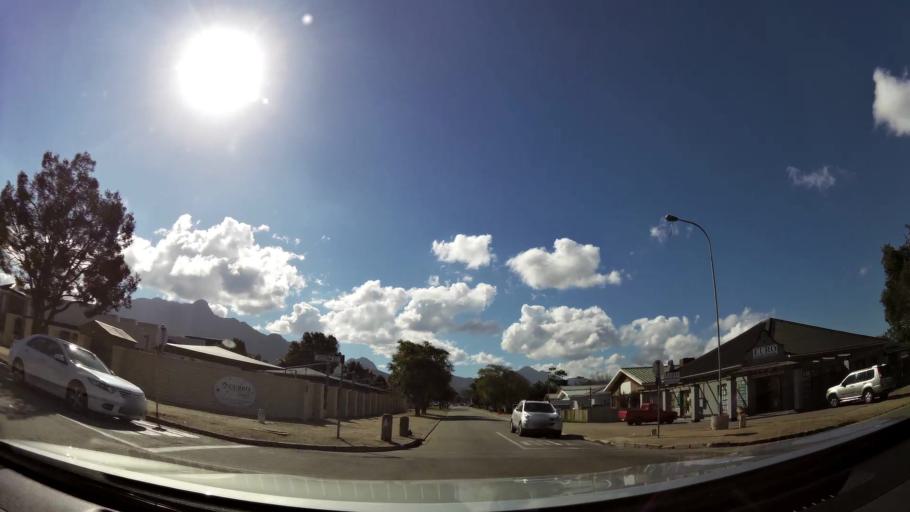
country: ZA
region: Western Cape
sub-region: Eden District Municipality
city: George
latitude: -33.9667
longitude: 22.4631
